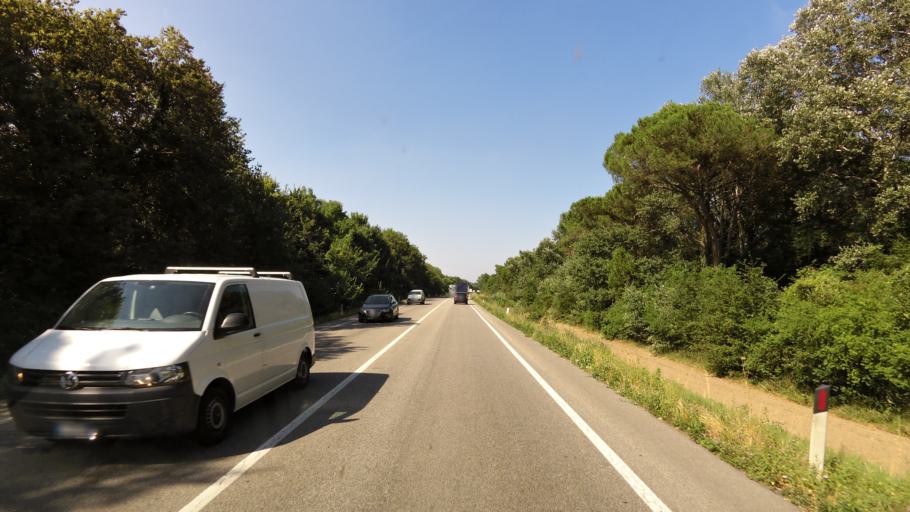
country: IT
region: Emilia-Romagna
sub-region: Provincia di Ravenna
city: Marina Romea
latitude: 44.4955
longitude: 12.2165
